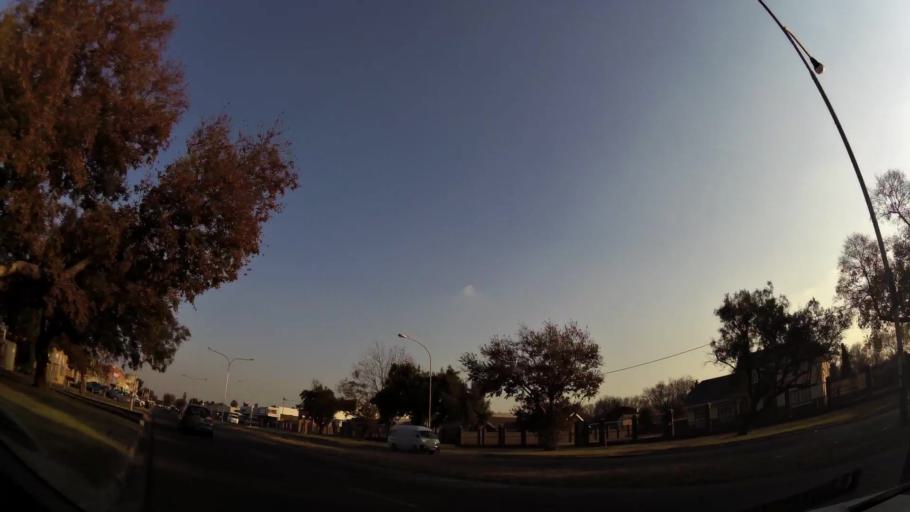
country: ZA
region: Gauteng
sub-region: Ekurhuleni Metropolitan Municipality
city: Springs
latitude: -26.3020
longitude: 28.4466
